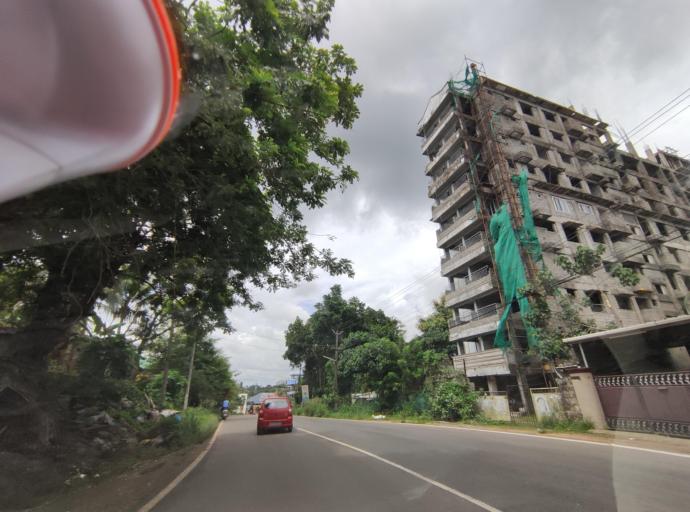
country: IN
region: Kerala
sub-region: Thiruvananthapuram
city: Nedumangad
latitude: 8.5754
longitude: 76.9431
